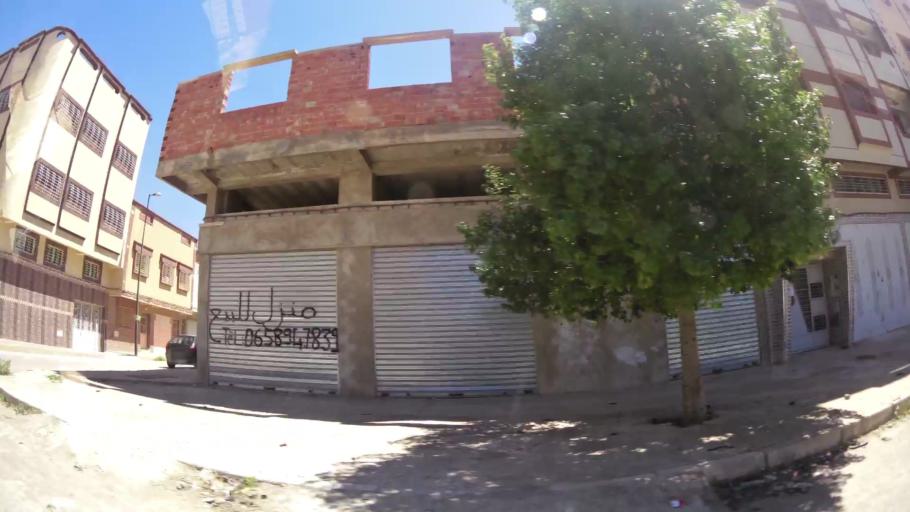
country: MA
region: Oriental
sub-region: Oujda-Angad
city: Oujda
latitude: 34.6808
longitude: -1.8669
